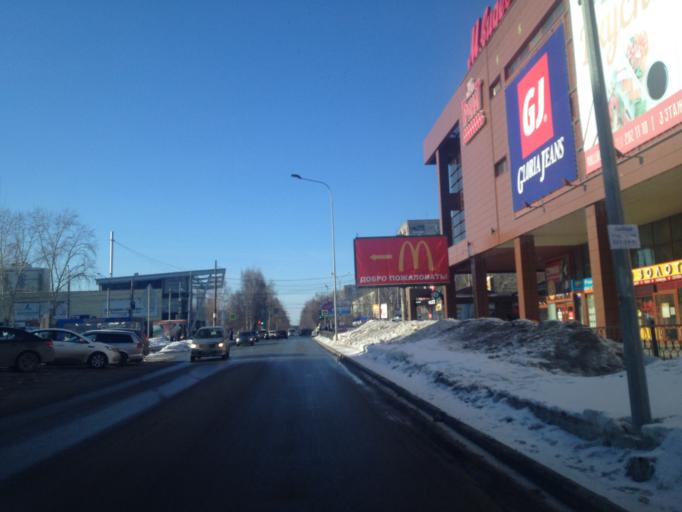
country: RU
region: Sverdlovsk
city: Sovkhoznyy
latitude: 56.7969
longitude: 60.5817
